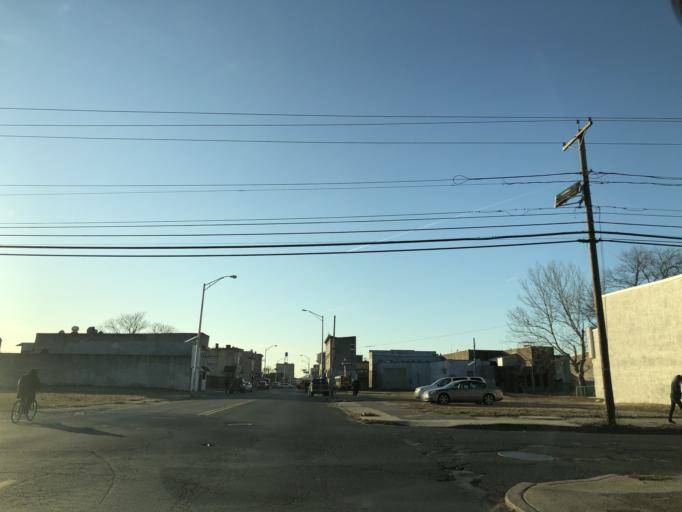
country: US
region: New Jersey
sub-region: Camden County
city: Camden
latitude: 39.9311
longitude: -75.1175
